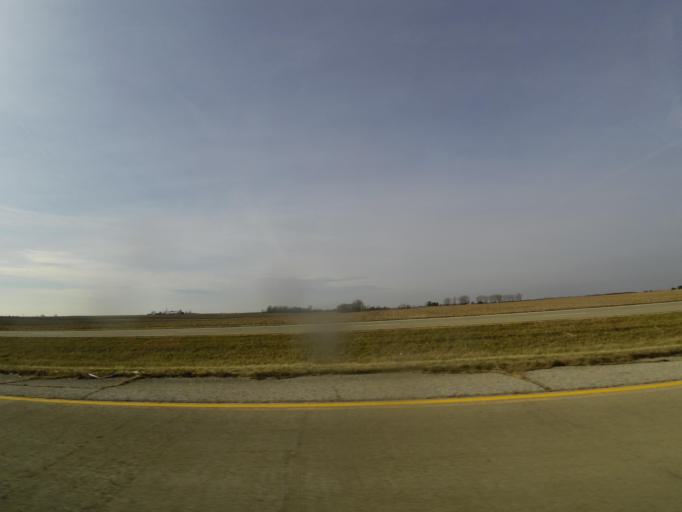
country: US
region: Illinois
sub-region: McLean County
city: Heyworth
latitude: 40.3974
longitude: -88.9902
